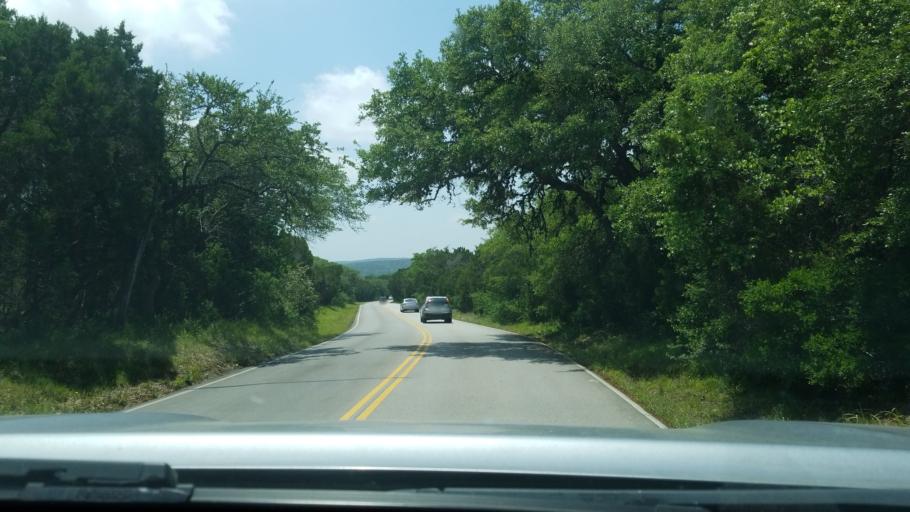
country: US
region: Texas
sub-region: Hays County
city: Woodcreek
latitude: 30.0407
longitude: -98.1119
